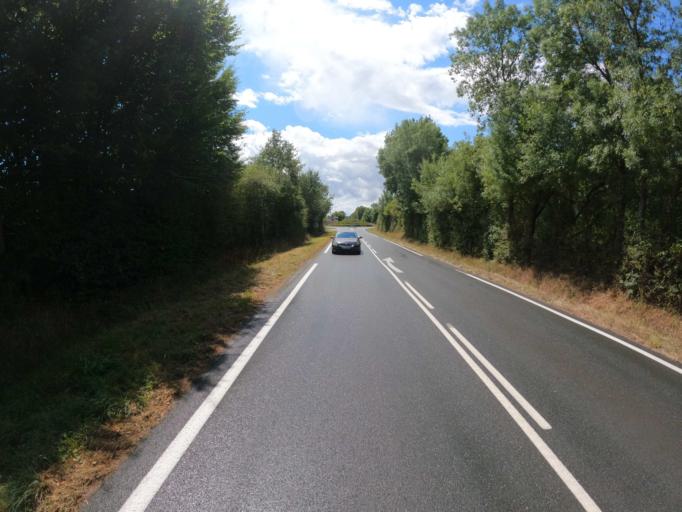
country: FR
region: Pays de la Loire
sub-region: Departement de Maine-et-Loire
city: Feneu
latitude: 47.6134
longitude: -0.5849
